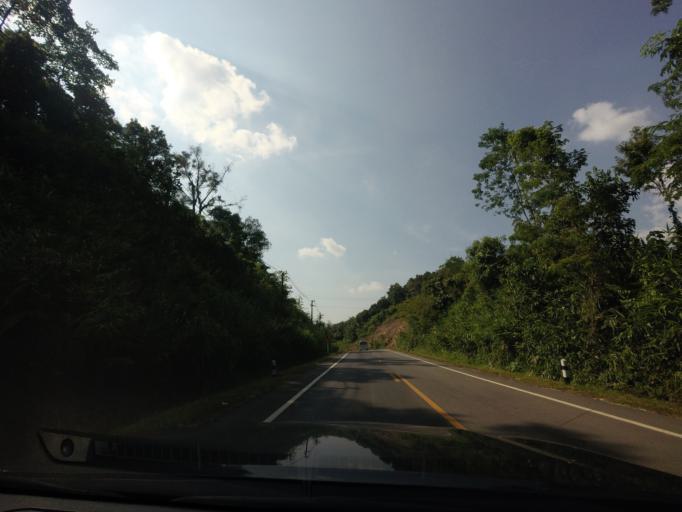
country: TH
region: Nan
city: Santi Suk
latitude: 18.9243
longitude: 100.9076
